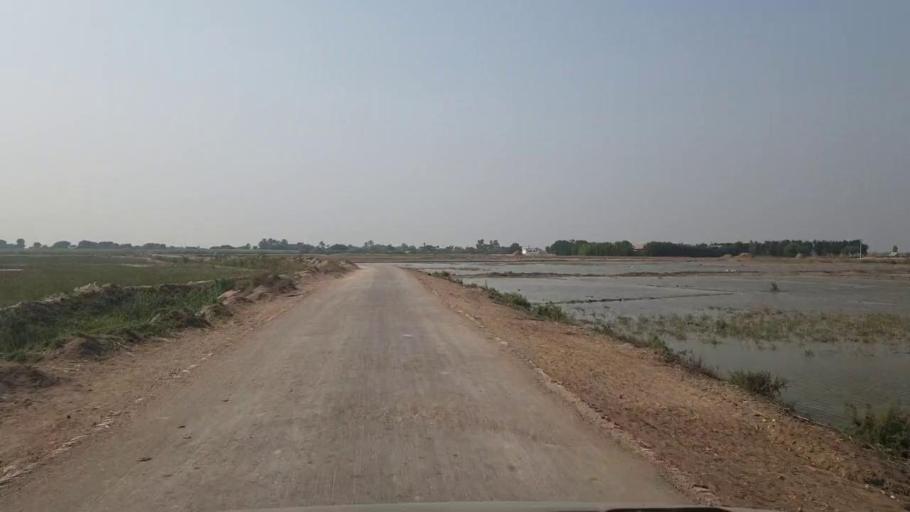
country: PK
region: Sindh
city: Tando Muhammad Khan
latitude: 25.0326
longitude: 68.3872
